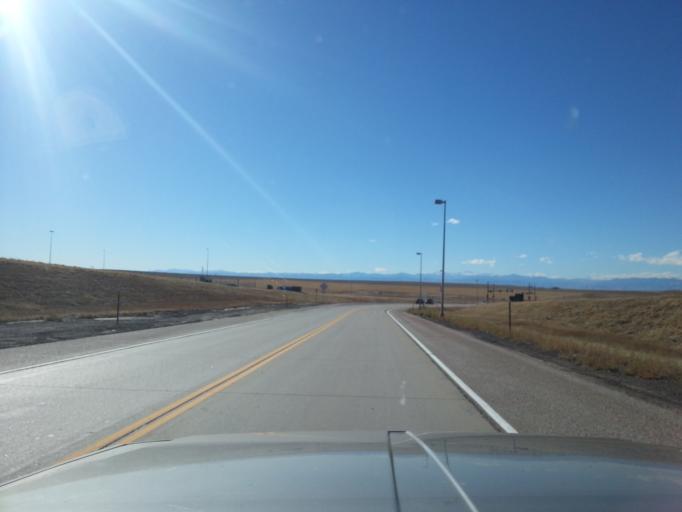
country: US
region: Colorado
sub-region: Adams County
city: Aurora
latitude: 39.8327
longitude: -104.7121
